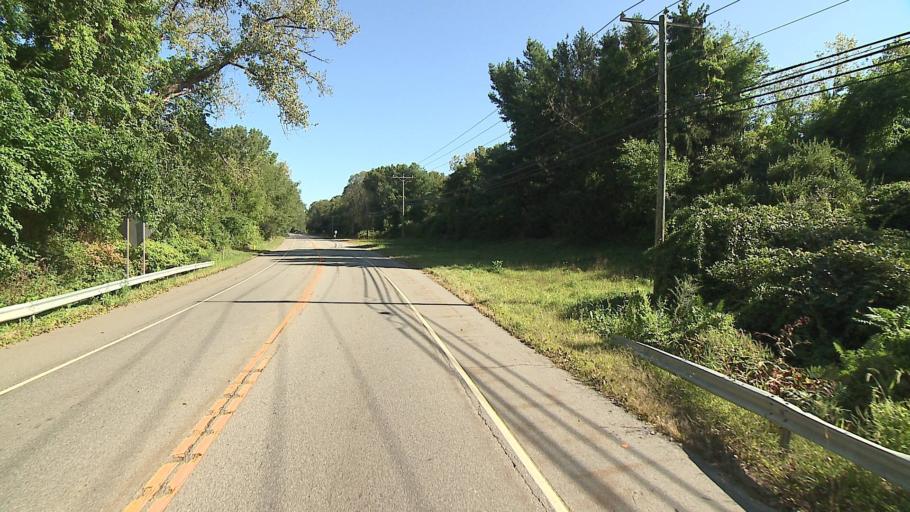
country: US
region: Connecticut
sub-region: New London County
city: Gales Ferry
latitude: 41.4435
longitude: -72.0775
